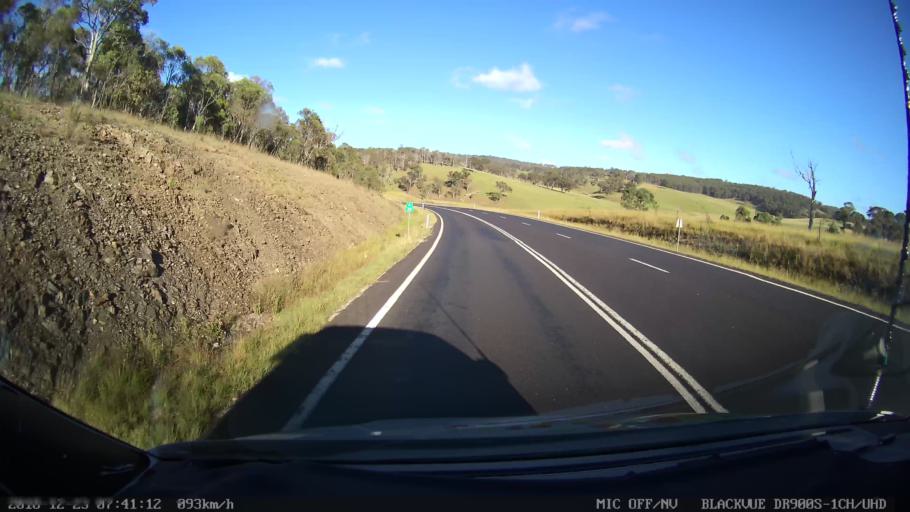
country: AU
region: New South Wales
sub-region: Armidale Dumaresq
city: Enmore
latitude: -30.5151
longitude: 151.9963
